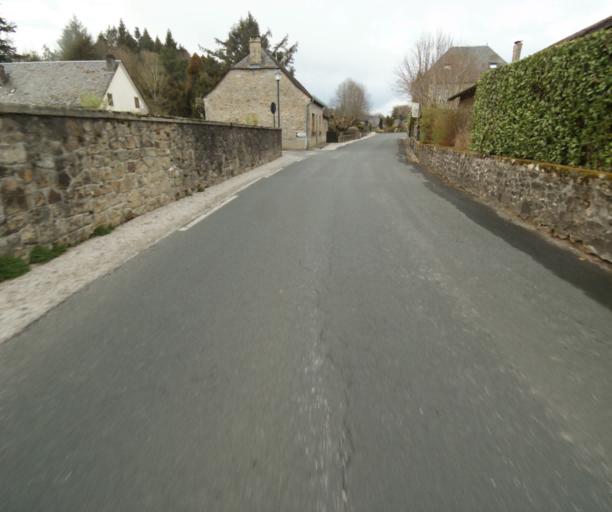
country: FR
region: Limousin
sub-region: Departement de la Correze
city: Saint-Privat
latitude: 45.2194
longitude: 2.0039
